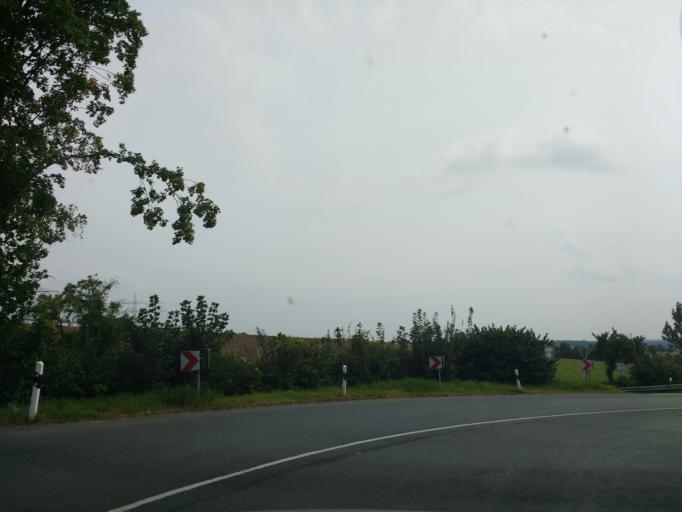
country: DE
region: North Rhine-Westphalia
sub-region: Regierungsbezirk Detmold
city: Paderborn
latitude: 51.6762
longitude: 8.7338
